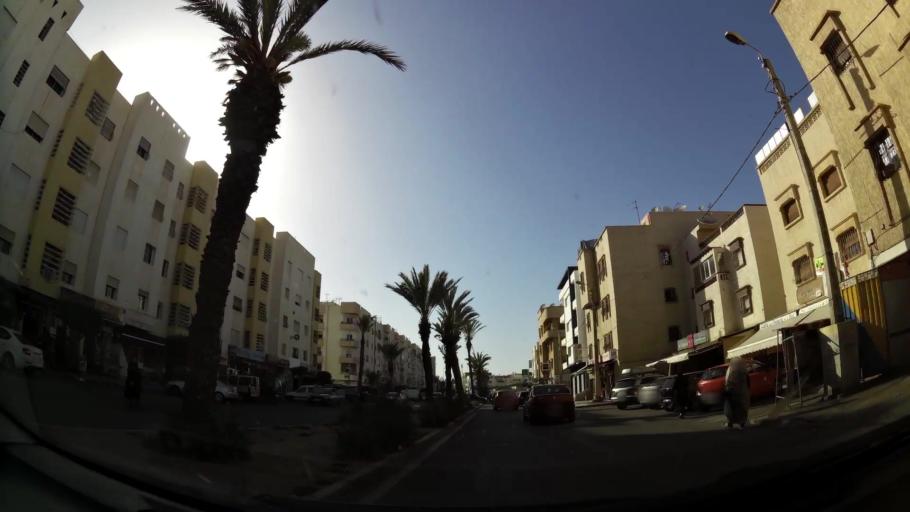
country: MA
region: Oued ed Dahab-Lagouira
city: Dakhla
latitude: 30.3977
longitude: -9.5492
